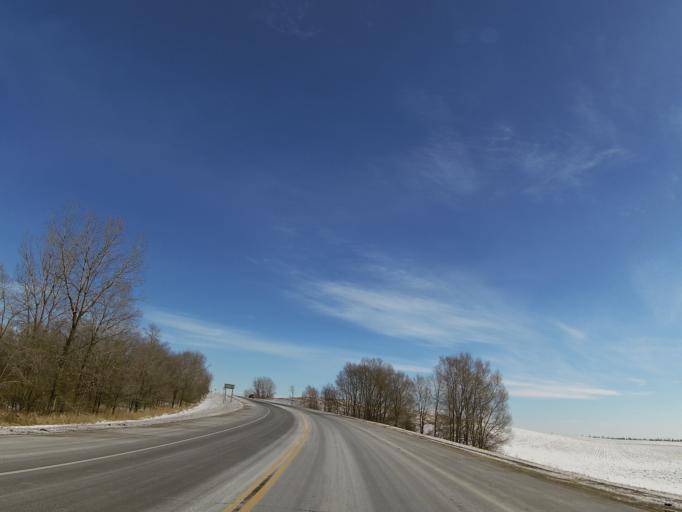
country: US
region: Minnesota
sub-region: Washington County
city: Cottage Grove
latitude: 44.7390
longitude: -92.9943
